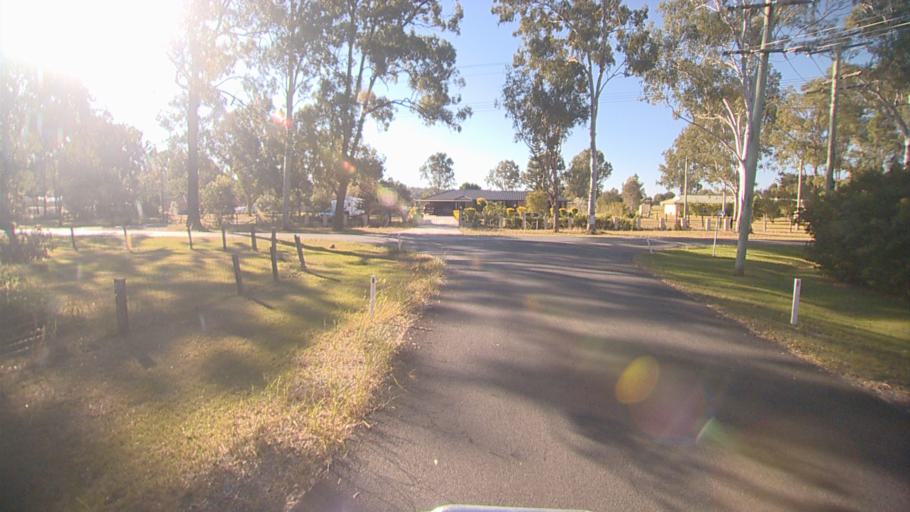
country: AU
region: Queensland
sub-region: Logan
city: Logan Reserve
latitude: -27.7419
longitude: 153.1089
